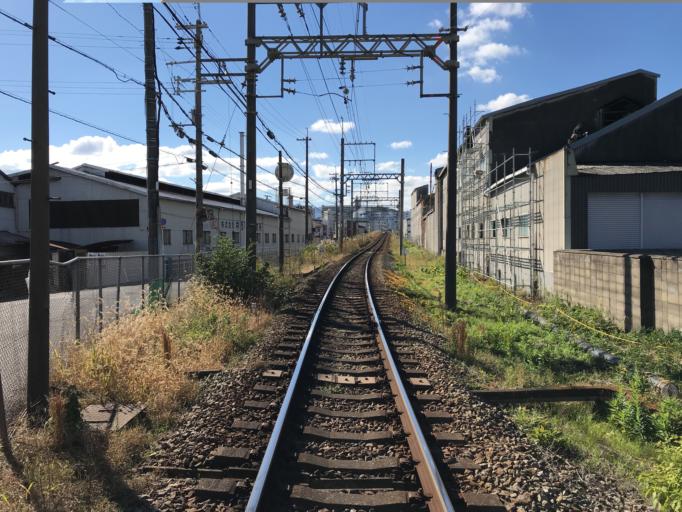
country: JP
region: Osaka
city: Tondabayashicho
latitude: 34.4553
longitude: 135.5767
